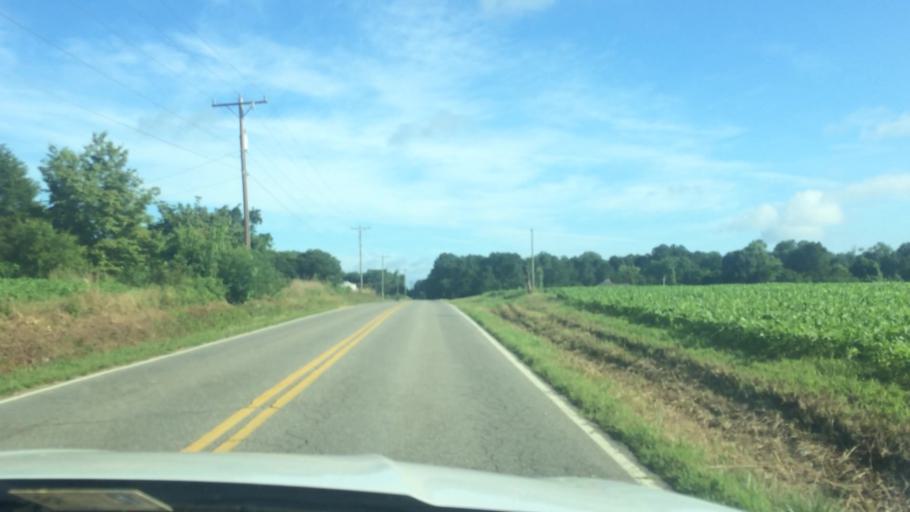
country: US
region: Virginia
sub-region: Middlesex County
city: Deltaville
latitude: 37.5695
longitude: -76.4536
